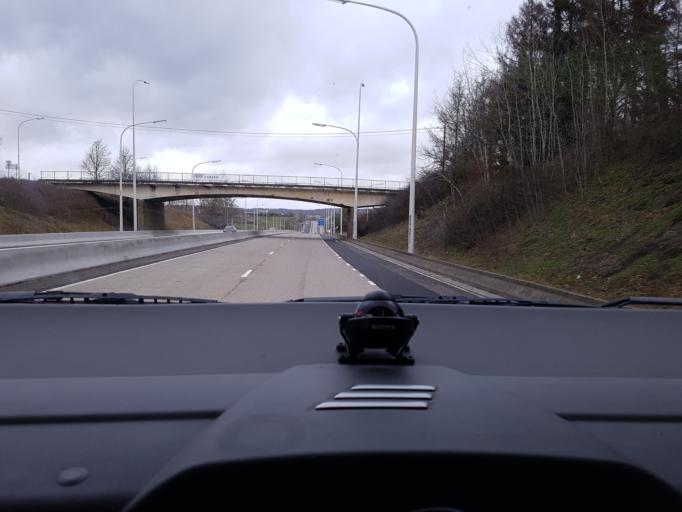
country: BE
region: Wallonia
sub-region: Province du Luxembourg
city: Marche-en-Famenne
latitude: 50.2676
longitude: 5.2462
